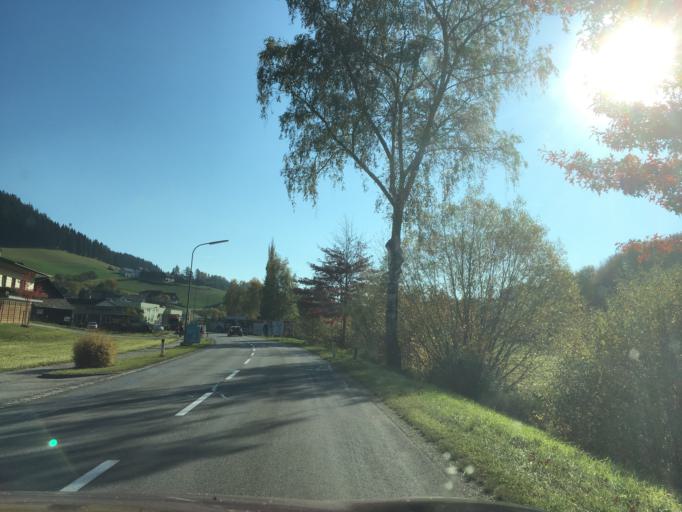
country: AT
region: Upper Austria
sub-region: Politischer Bezirk Perg
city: Sankt Georgen am Walde
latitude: 48.4355
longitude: 14.7799
